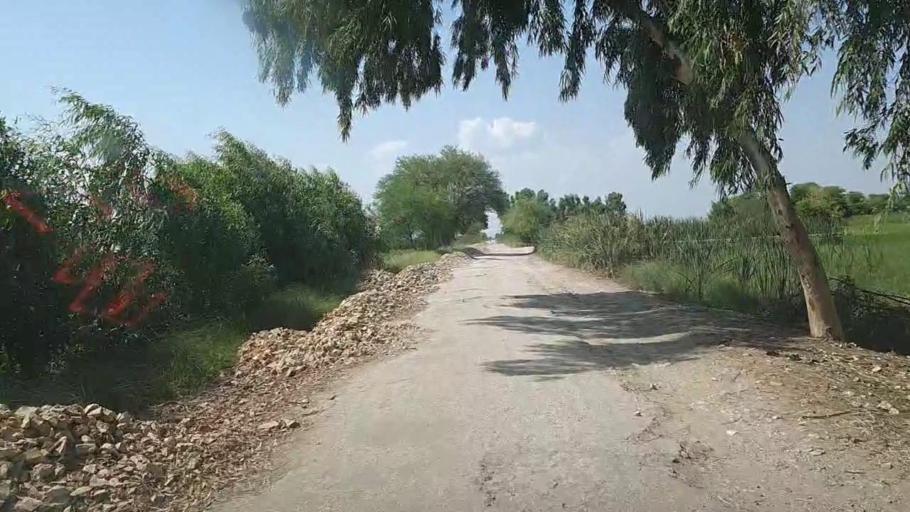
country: PK
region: Sindh
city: Khairpur
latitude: 28.0883
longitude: 69.6323
